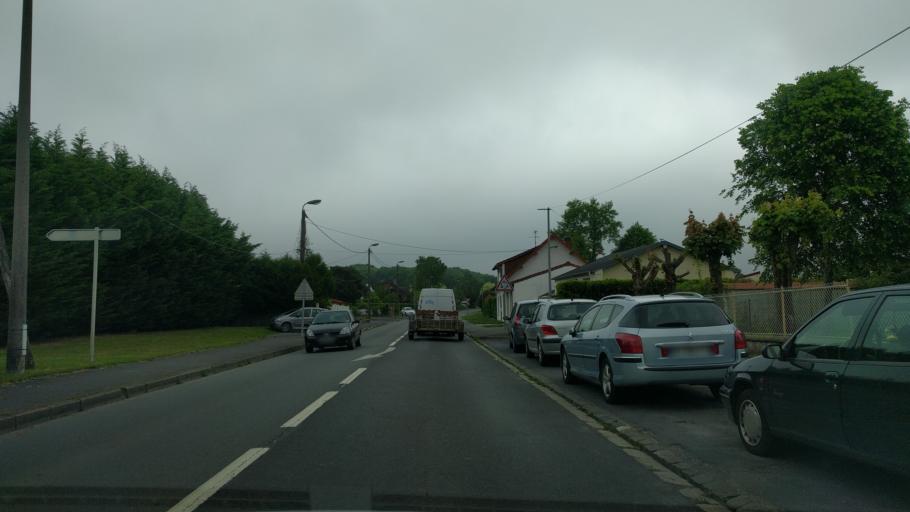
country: FR
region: Picardie
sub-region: Departement de la Somme
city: Peronne
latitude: 49.9415
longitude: 2.9336
